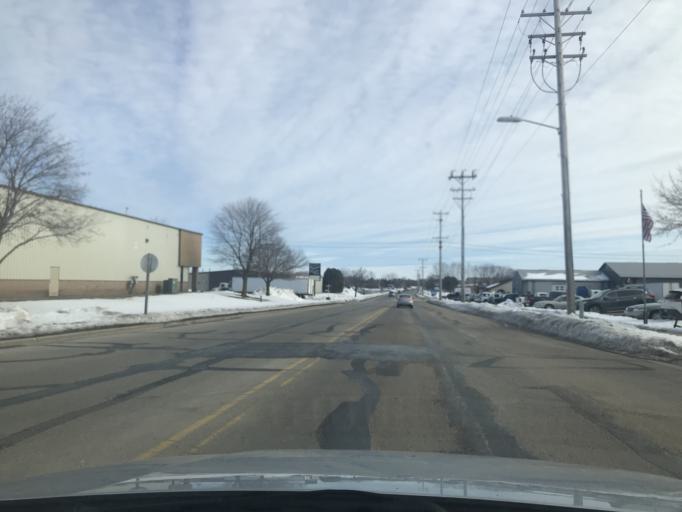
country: US
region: Wisconsin
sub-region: Oconto County
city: Oconto Falls
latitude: 44.8827
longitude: -88.1460
